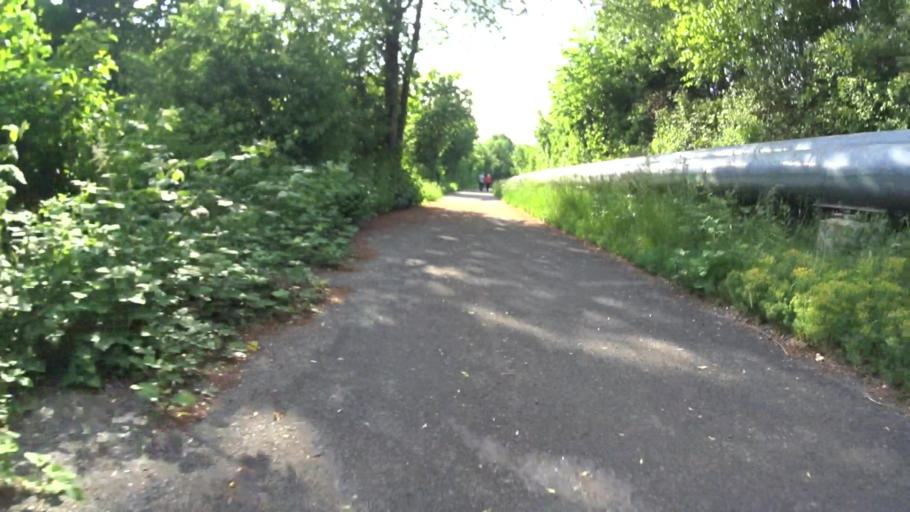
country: DE
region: Baden-Wuerttemberg
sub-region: Regierungsbezirk Stuttgart
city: Altbach
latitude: 48.7182
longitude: 9.3849
